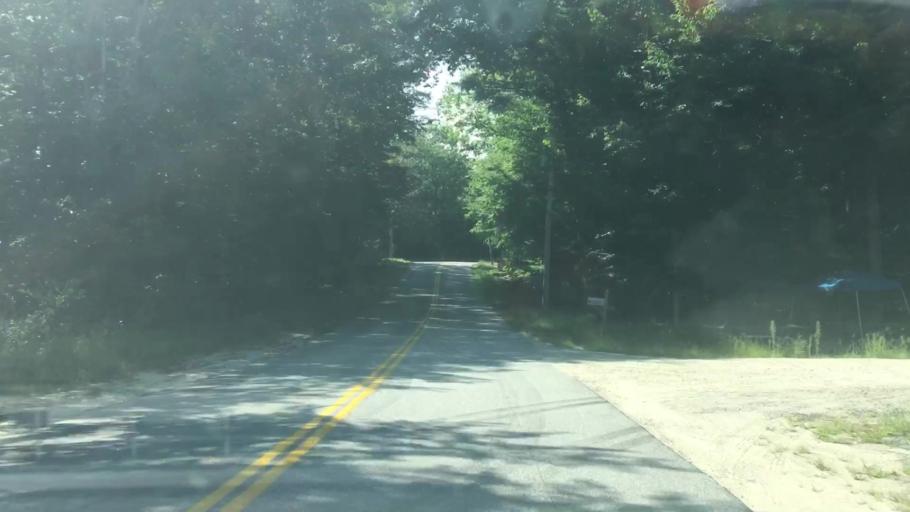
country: US
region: Maine
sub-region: Androscoggin County
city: Poland
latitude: 44.0142
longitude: -70.3909
